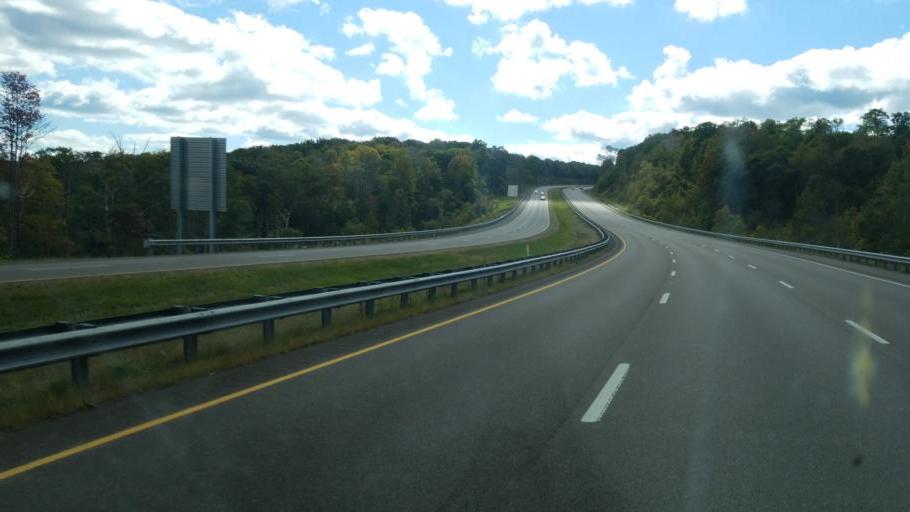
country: US
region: Pennsylvania
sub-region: Somerset County
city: Meyersdale
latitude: 39.6931
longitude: -79.1852
